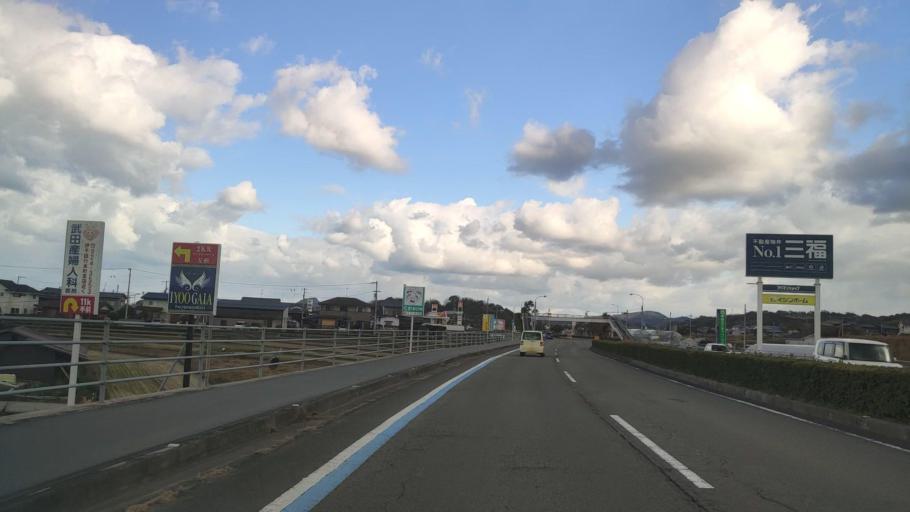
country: JP
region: Ehime
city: Hojo
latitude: 33.9417
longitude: 132.7744
